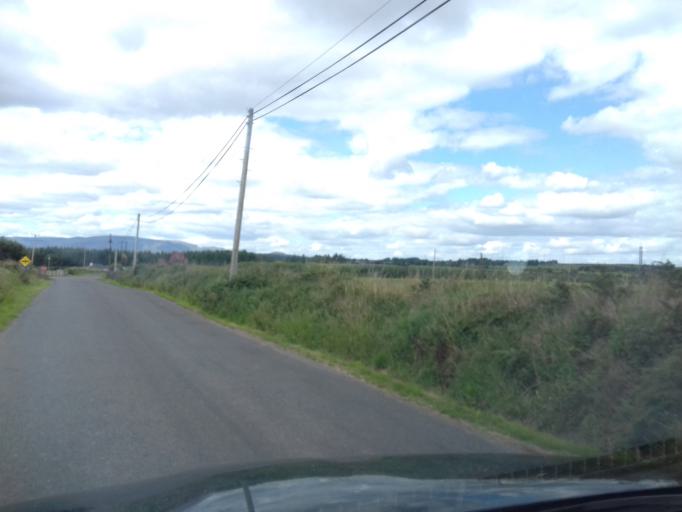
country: IE
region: Munster
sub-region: Waterford
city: Portlaw
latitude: 52.1819
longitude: -7.2984
